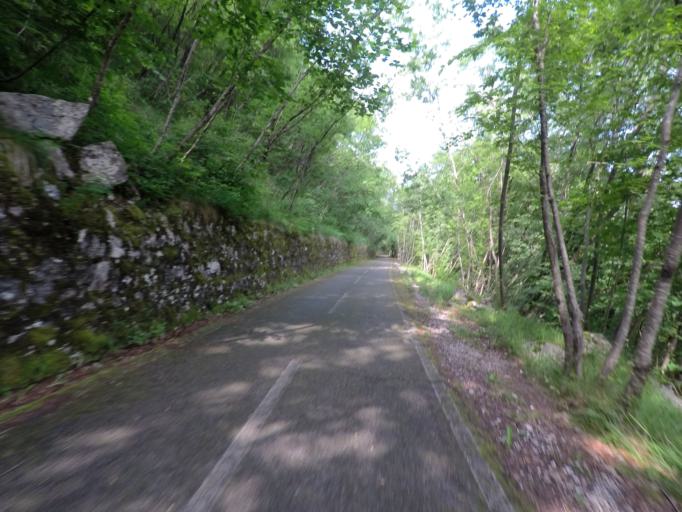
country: IT
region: Friuli Venezia Giulia
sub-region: Provincia di Udine
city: Amaro
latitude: 46.3603
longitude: 13.0965
